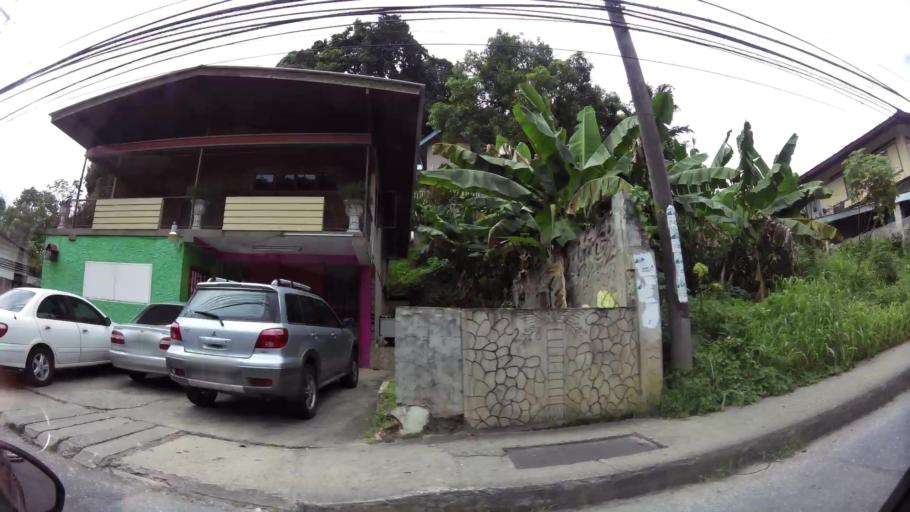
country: TT
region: Diego Martin
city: Petit Valley
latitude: 10.7097
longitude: -61.5140
